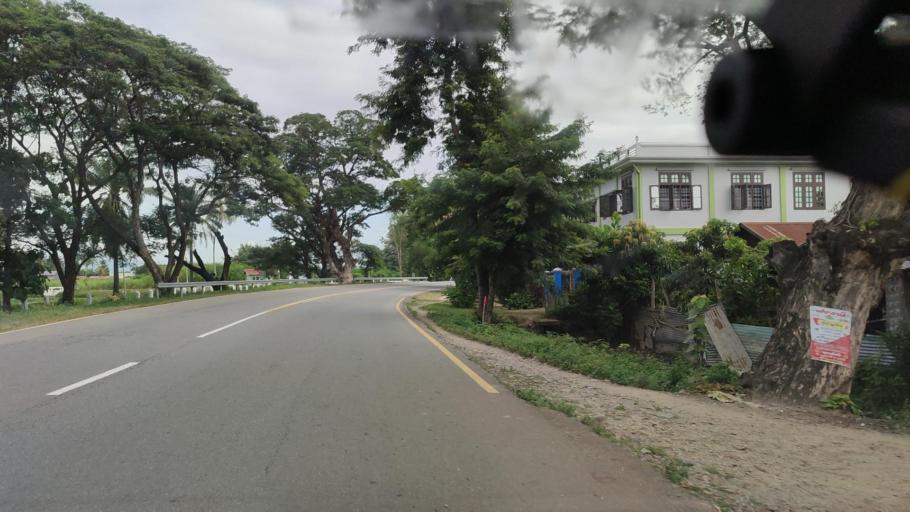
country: MM
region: Mandalay
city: Pyinmana
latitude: 19.8152
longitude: 96.2655
